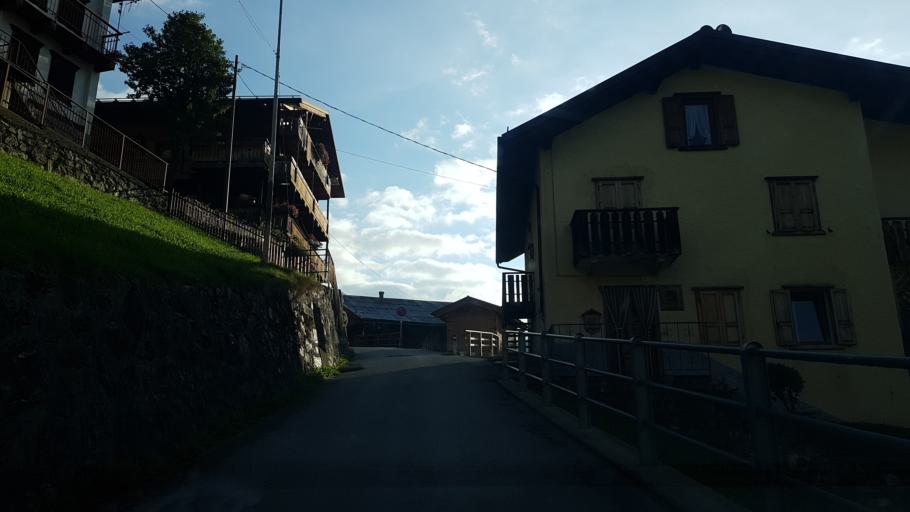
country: IT
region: Veneto
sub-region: Provincia di Belluno
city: San Pietro di Cadore
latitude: 46.5811
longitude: 12.5766
